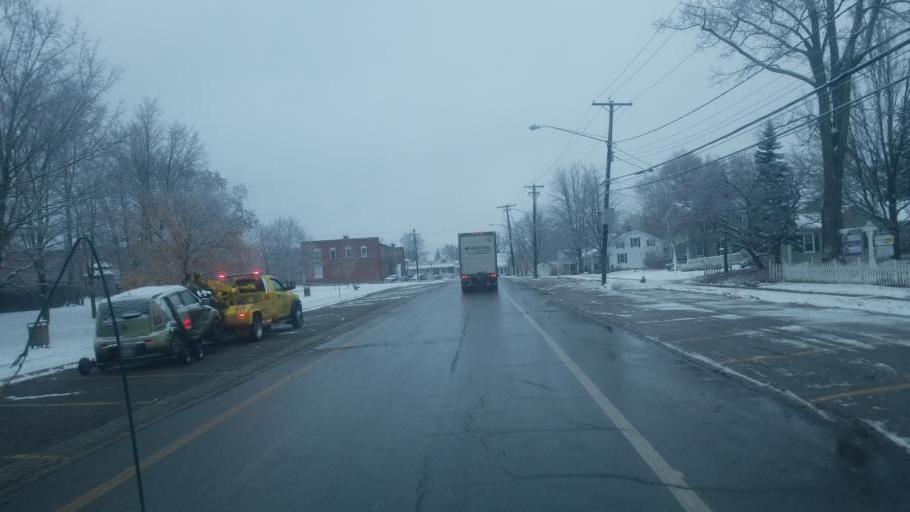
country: US
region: Ohio
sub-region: Geauga County
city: Burton
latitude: 41.4714
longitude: -81.1444
